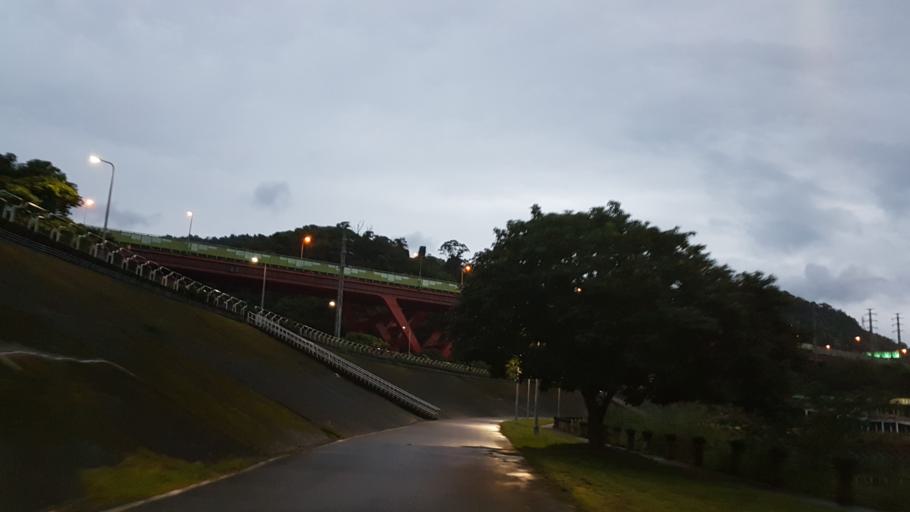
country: TW
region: Taipei
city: Taipei
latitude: 24.9779
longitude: 121.5579
